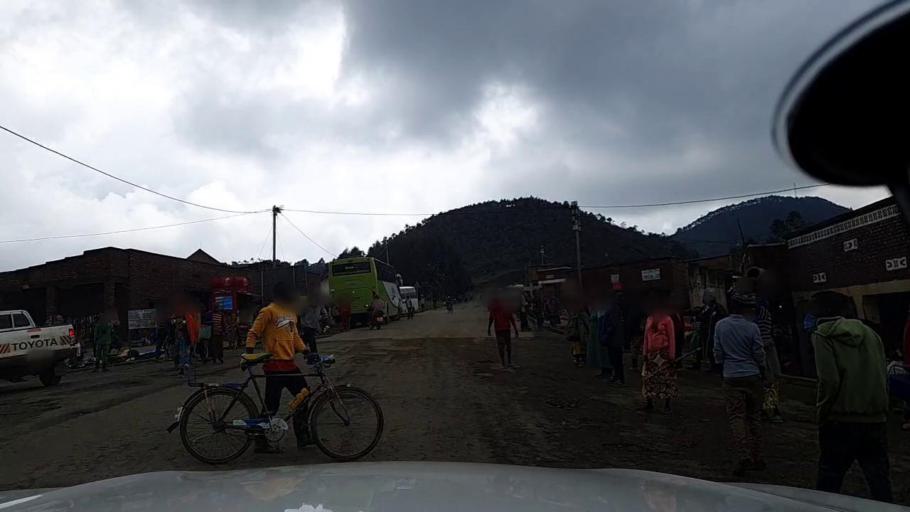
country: RW
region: Western Province
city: Kibuye
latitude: -2.0582
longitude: 29.5100
